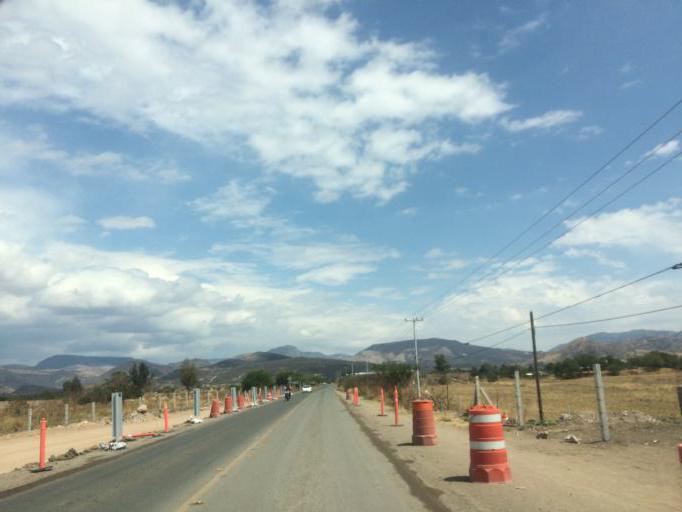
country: MX
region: Guanajuato
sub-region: Leon
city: Ladrilleras del Refugio
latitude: 21.0783
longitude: -101.5452
